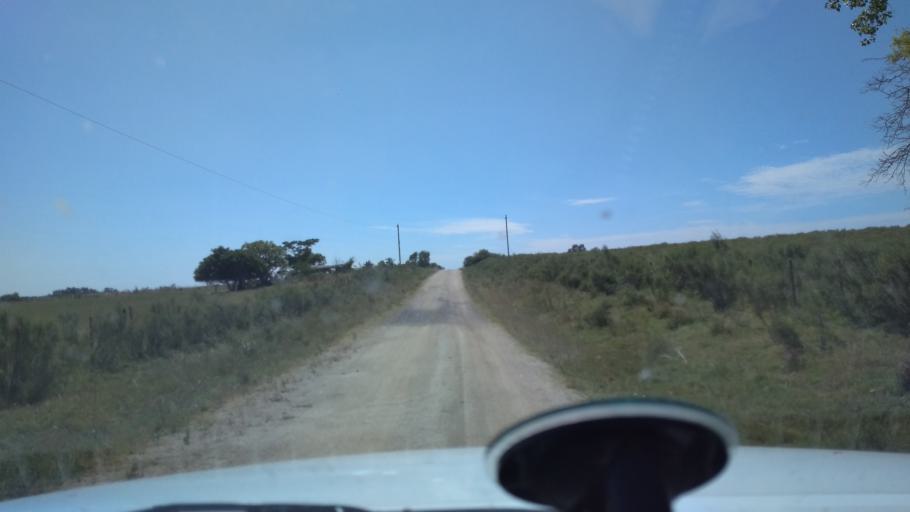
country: UY
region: Canelones
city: San Ramon
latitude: -34.1514
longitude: -55.8375
